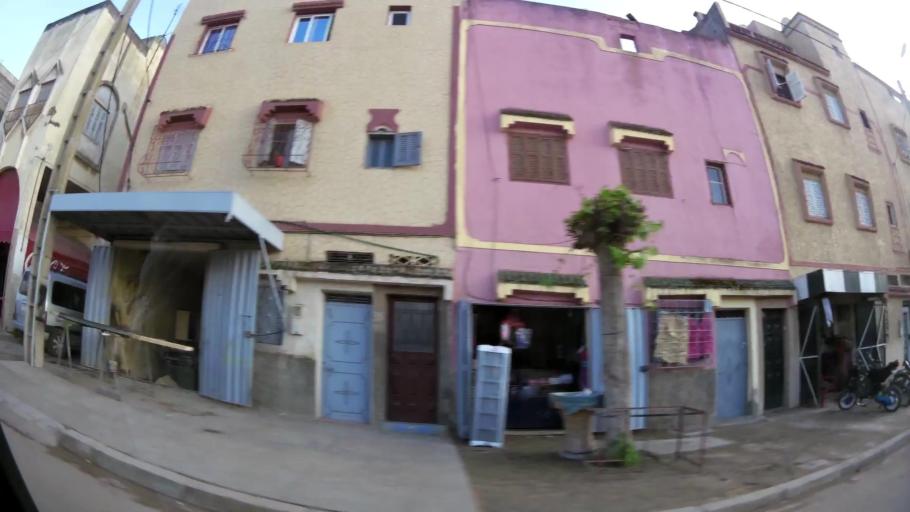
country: MA
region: Chaouia-Ouardigha
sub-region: Settat Province
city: Settat
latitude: 33.0020
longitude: -7.6372
